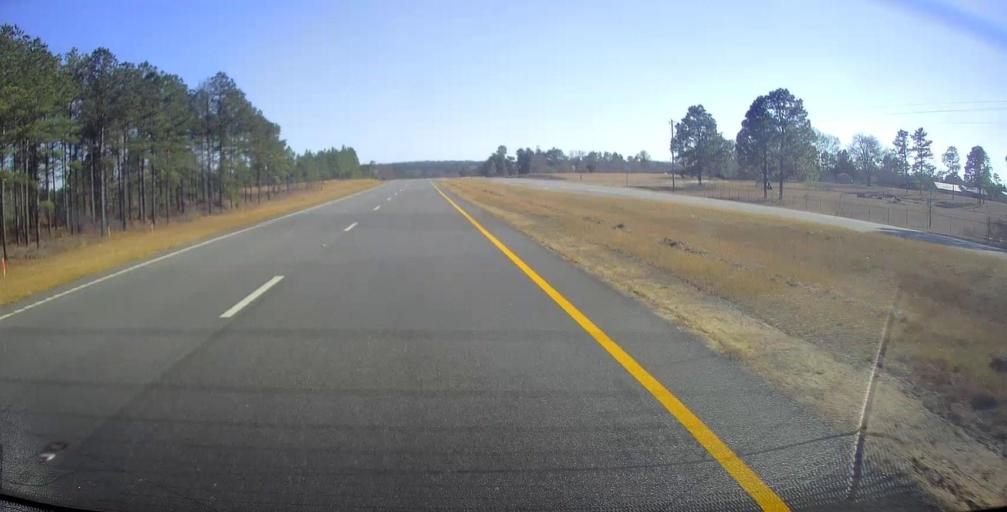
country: US
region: Georgia
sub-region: Taylor County
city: Butler
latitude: 32.5943
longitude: -84.2383
